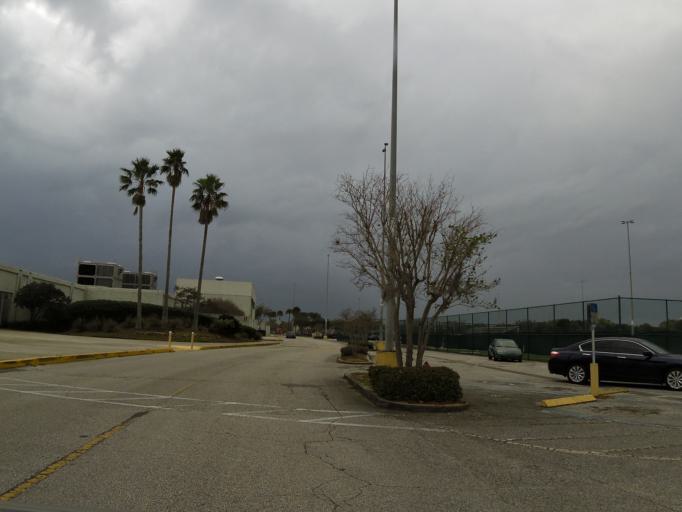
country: US
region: Florida
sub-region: Duval County
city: Jacksonville
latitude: 30.3243
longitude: -81.5489
